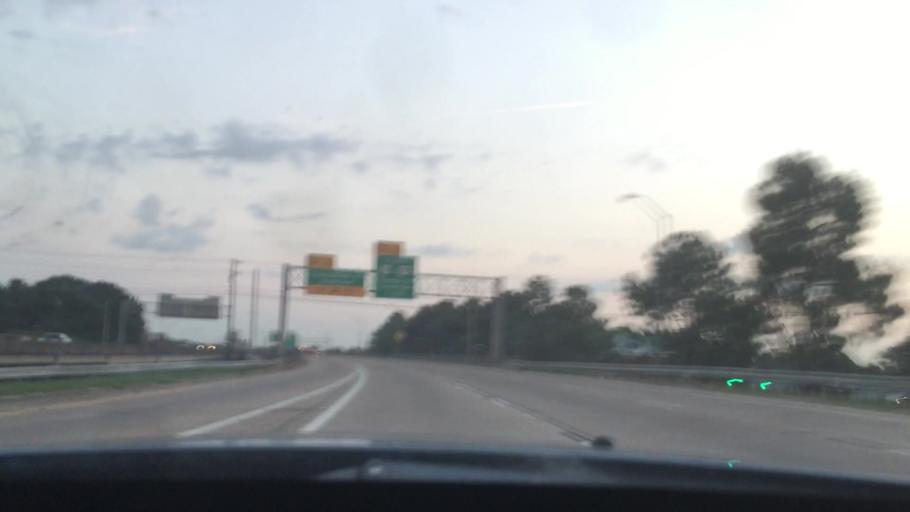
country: US
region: Louisiana
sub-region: East Baton Rouge Parish
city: Baton Rouge
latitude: 30.4425
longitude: -91.1783
